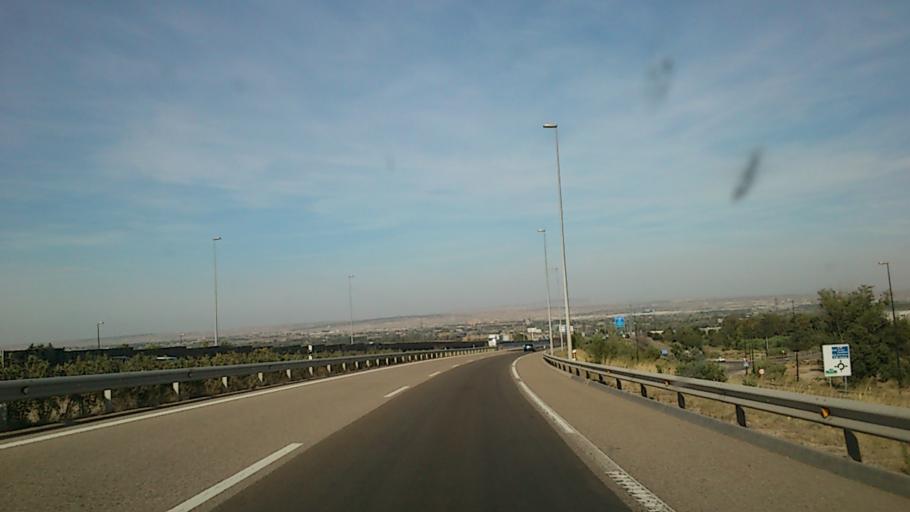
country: ES
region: Aragon
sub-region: Provincia de Zaragoza
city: Zaragoza
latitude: 41.6200
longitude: -0.8644
